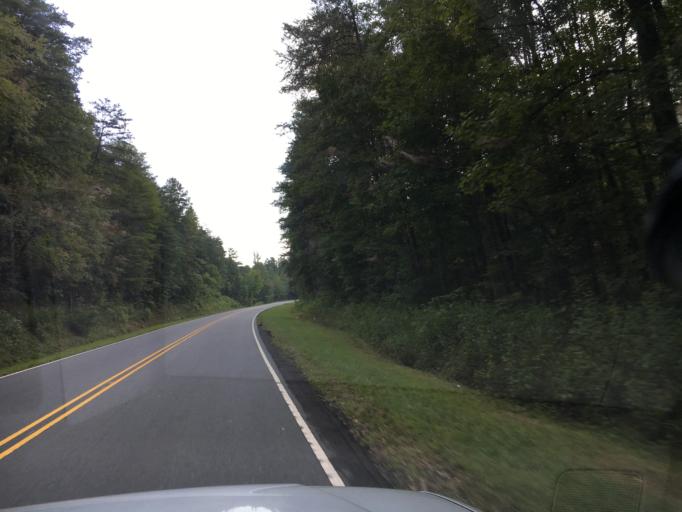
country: US
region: North Carolina
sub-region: Rutherford County
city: Rutherfordton
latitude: 35.4583
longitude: -81.9789
